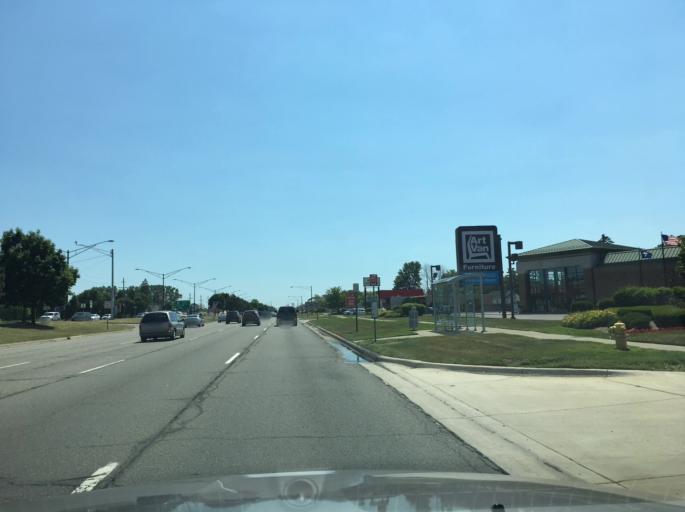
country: US
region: Michigan
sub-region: Macomb County
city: Clinton
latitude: 42.5455
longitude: -82.9054
